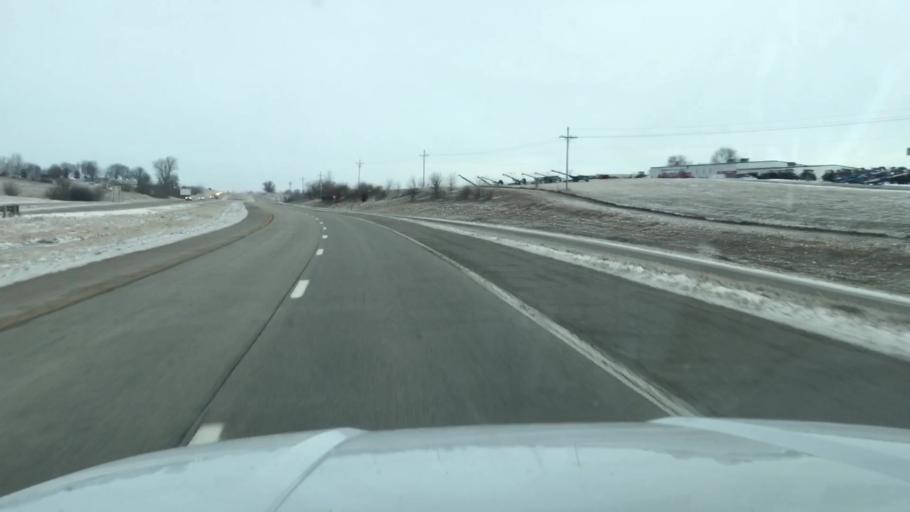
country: US
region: Missouri
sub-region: Andrew County
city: Savannah
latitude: 39.9626
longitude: -94.8620
